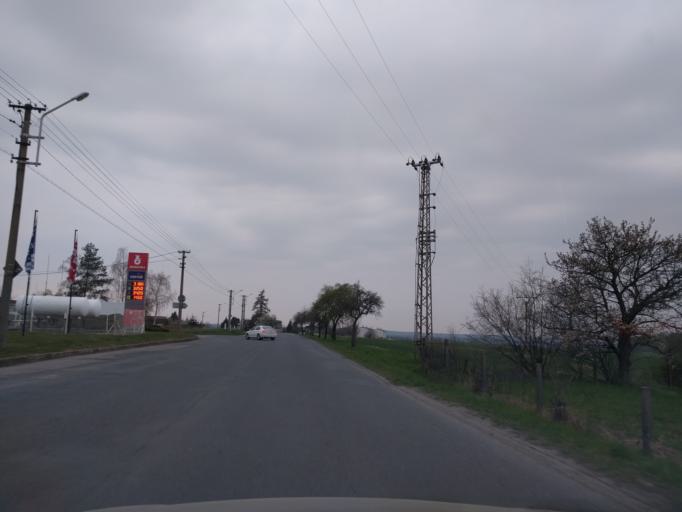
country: CZ
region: Central Bohemia
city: Kostelec nad Cernymi Lesy
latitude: 49.9929
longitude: 14.8444
